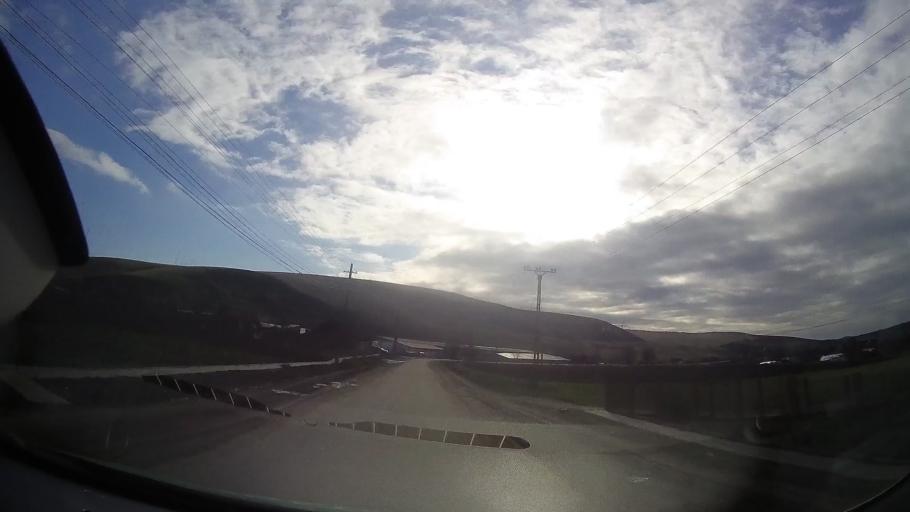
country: RO
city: Barza
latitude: 46.5505
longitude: 24.1287
